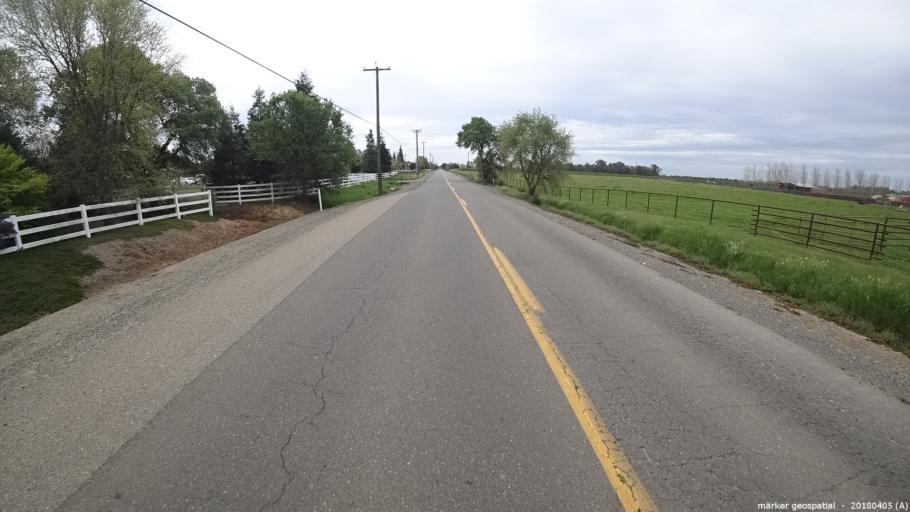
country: US
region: California
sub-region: Sacramento County
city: Galt
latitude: 38.2748
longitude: -121.3373
